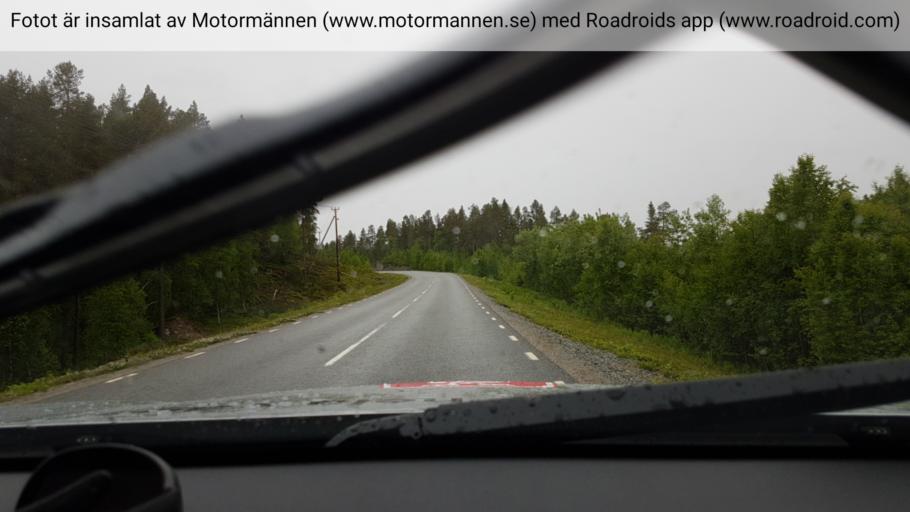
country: SE
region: Vaesterbotten
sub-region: Storumans Kommun
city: Fristad
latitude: 65.9435
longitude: 16.2636
